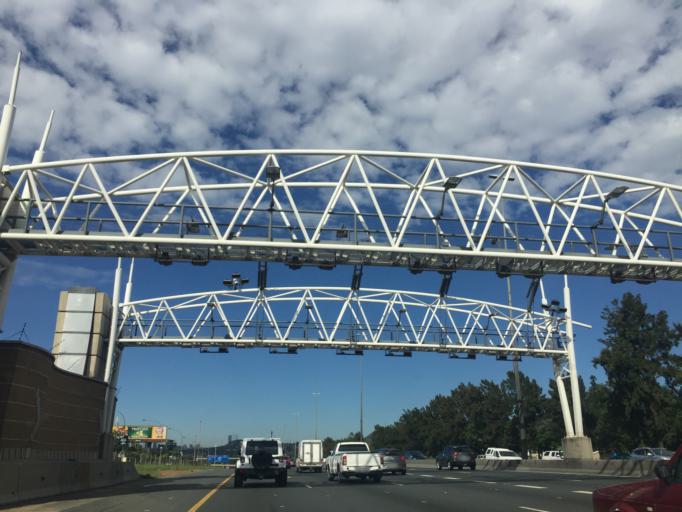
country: ZA
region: Gauteng
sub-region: Ekurhuleni Metropolitan Municipality
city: Germiston
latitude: -26.1670
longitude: 28.1410
